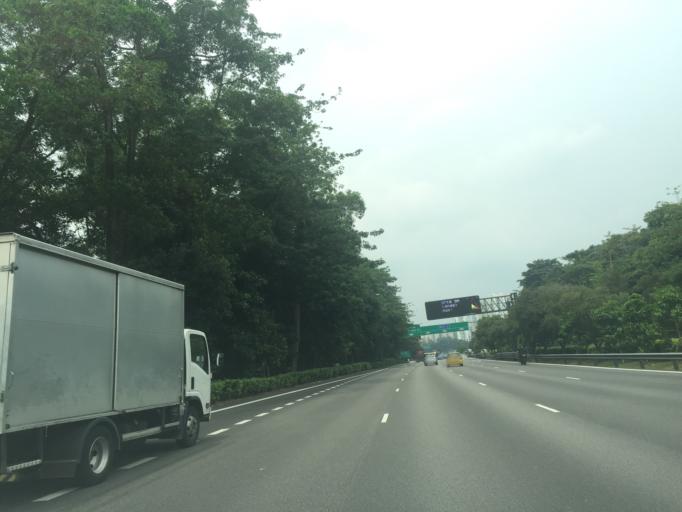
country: MY
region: Johor
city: Johor Bahru
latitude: 1.3898
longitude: 103.7495
